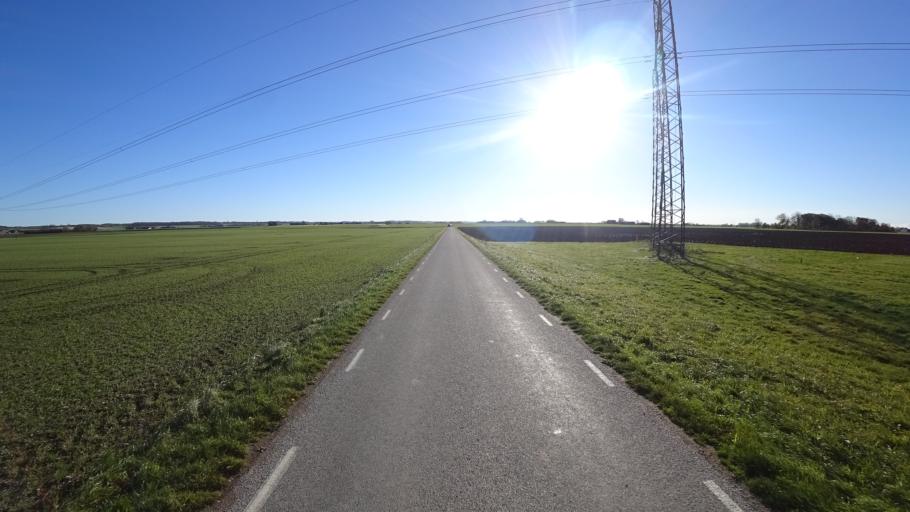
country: SE
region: Skane
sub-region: Staffanstorps Kommun
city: Staffanstorp
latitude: 55.6713
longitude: 13.2625
